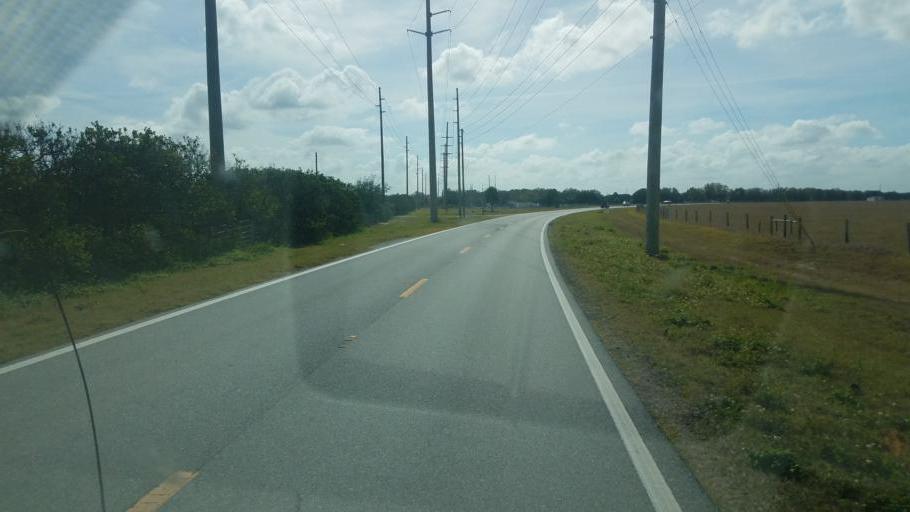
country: US
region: Florida
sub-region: Polk County
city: Lake Wales
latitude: 27.9296
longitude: -81.5375
